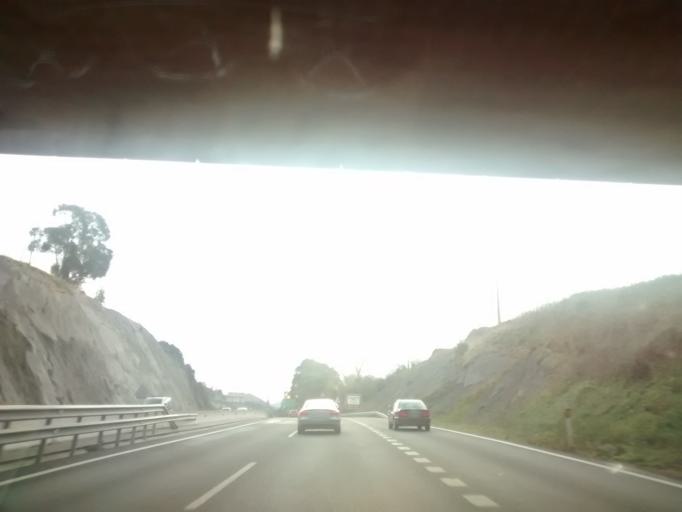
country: ES
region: Basque Country
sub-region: Bizkaia
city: San Julian de Muskiz
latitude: 43.3430
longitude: -3.1565
